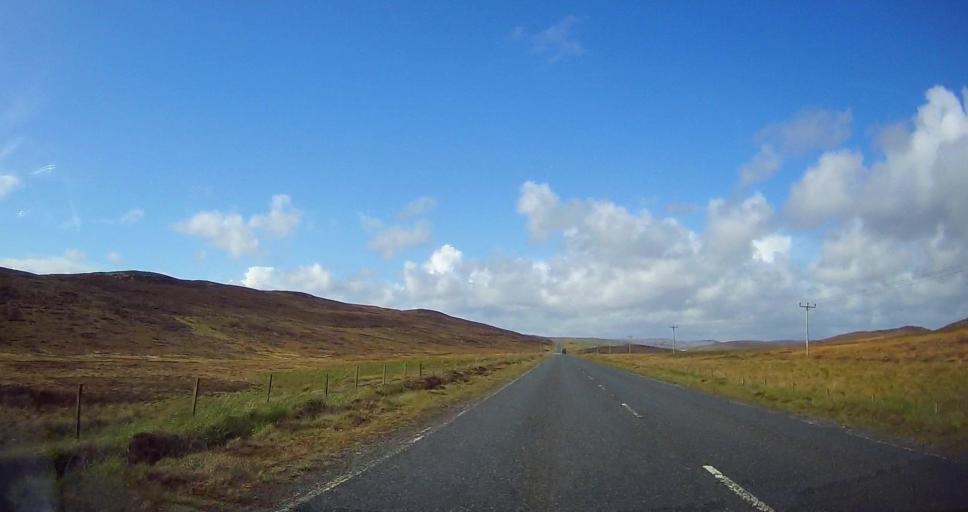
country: GB
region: Scotland
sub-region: Shetland Islands
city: Lerwick
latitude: 60.2065
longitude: -1.2333
